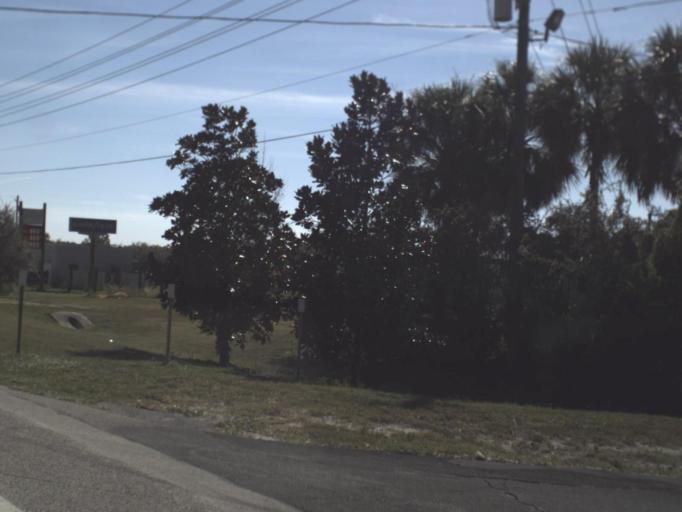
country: US
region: Florida
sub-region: Highlands County
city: Lake Placid
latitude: 27.2878
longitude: -81.3582
